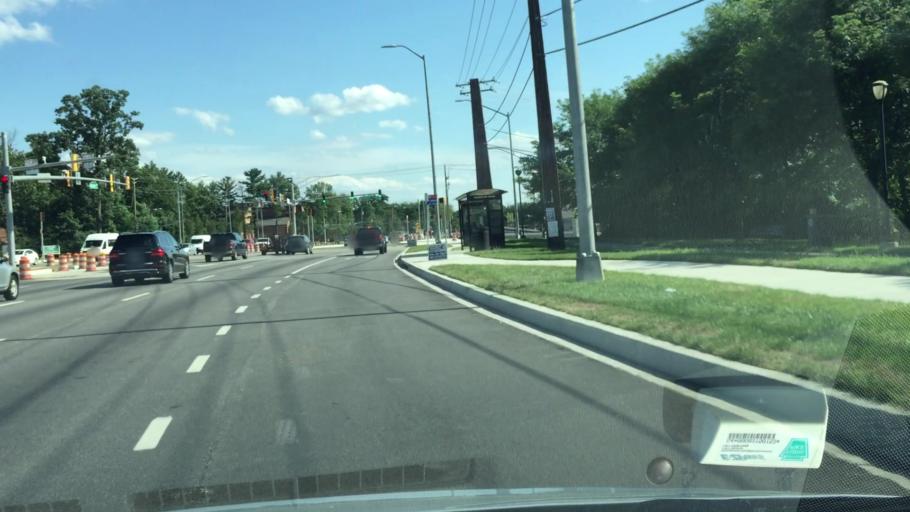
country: US
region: Maryland
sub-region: Montgomery County
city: Glenmont
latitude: 39.0588
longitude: -77.0503
